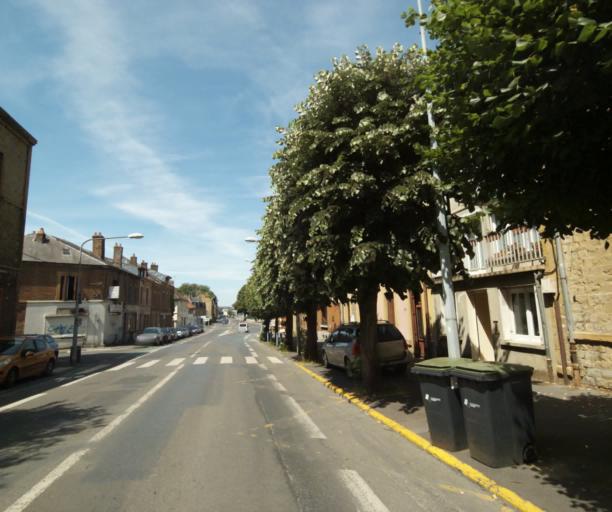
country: FR
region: Champagne-Ardenne
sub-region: Departement des Ardennes
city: Charleville-Mezieres
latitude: 49.7544
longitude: 4.7231
